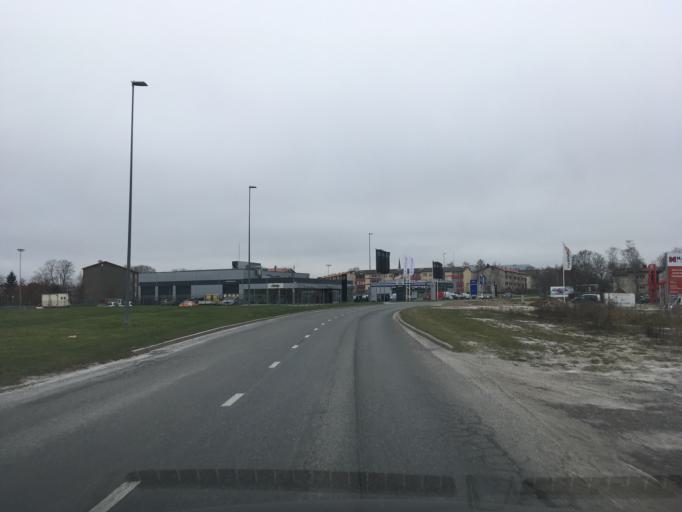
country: EE
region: Ida-Virumaa
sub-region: Johvi vald
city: Johvi
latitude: 59.3661
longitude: 27.4166
